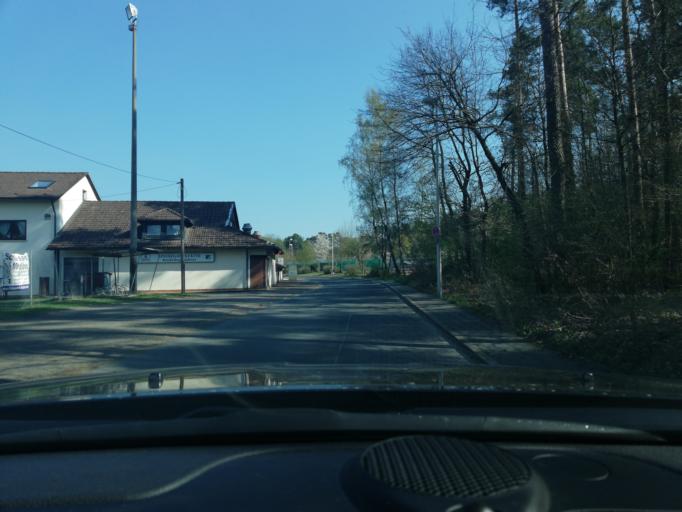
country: DE
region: Bavaria
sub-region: Regierungsbezirk Mittelfranken
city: Hessdorf
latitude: 49.6327
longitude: 10.9444
